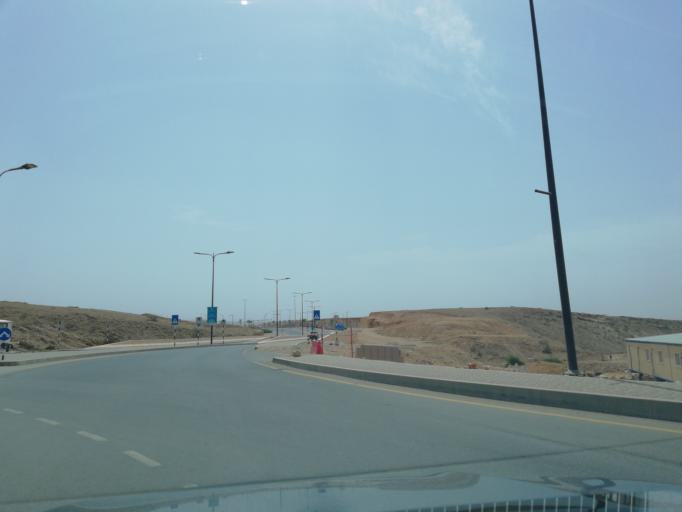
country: OM
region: Muhafazat Masqat
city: Bawshar
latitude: 23.5780
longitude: 58.3279
